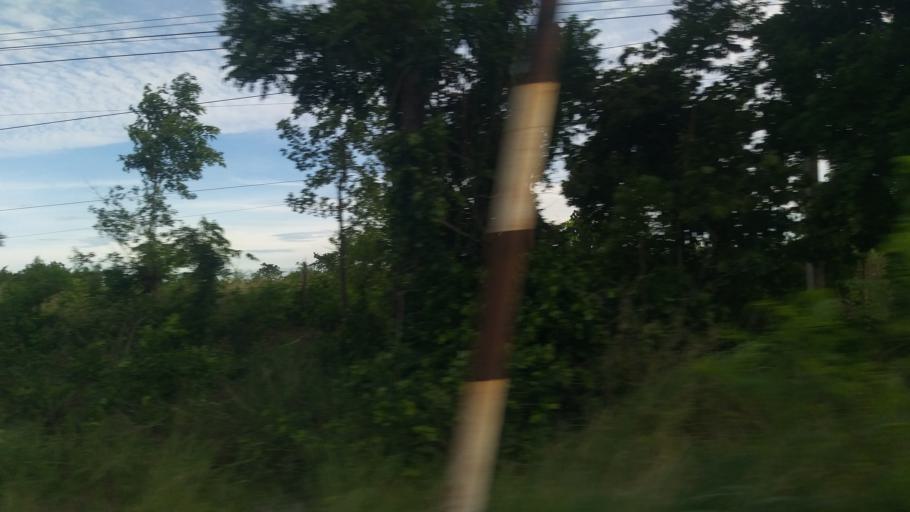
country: TH
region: Chaiyaphum
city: Phu Khiao
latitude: 16.3245
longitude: 102.2088
